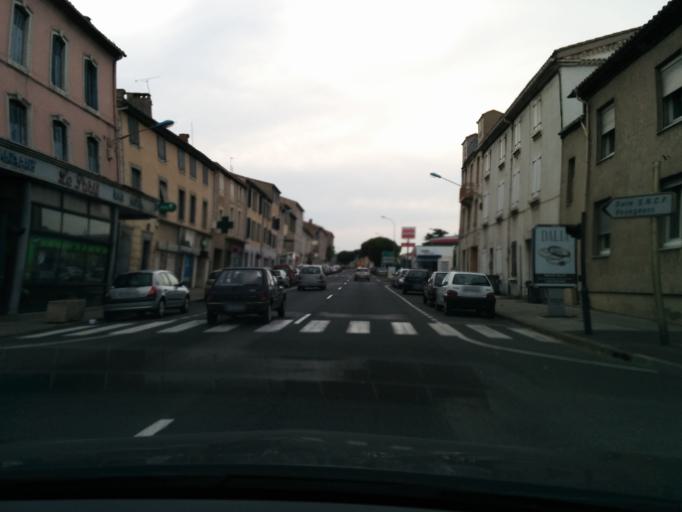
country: FR
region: Languedoc-Roussillon
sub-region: Departement de l'Aude
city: Carcassonne
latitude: 43.2168
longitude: 2.3481
